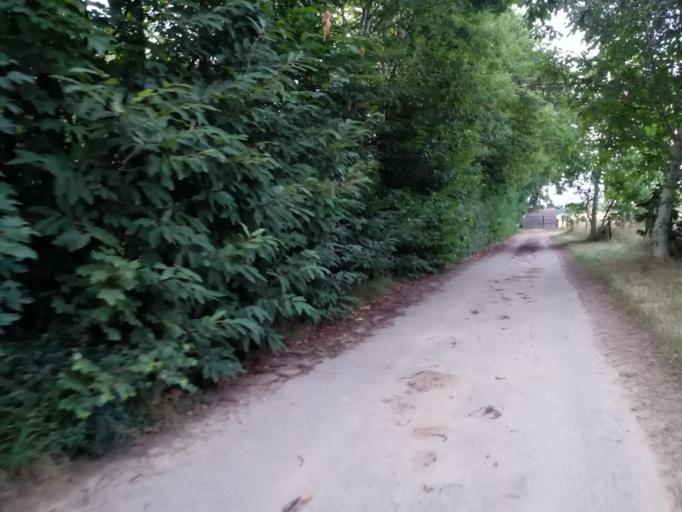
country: BE
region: Flanders
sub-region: Provincie Vlaams-Brabant
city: Oud-Heverlee
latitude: 50.8292
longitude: 4.7044
